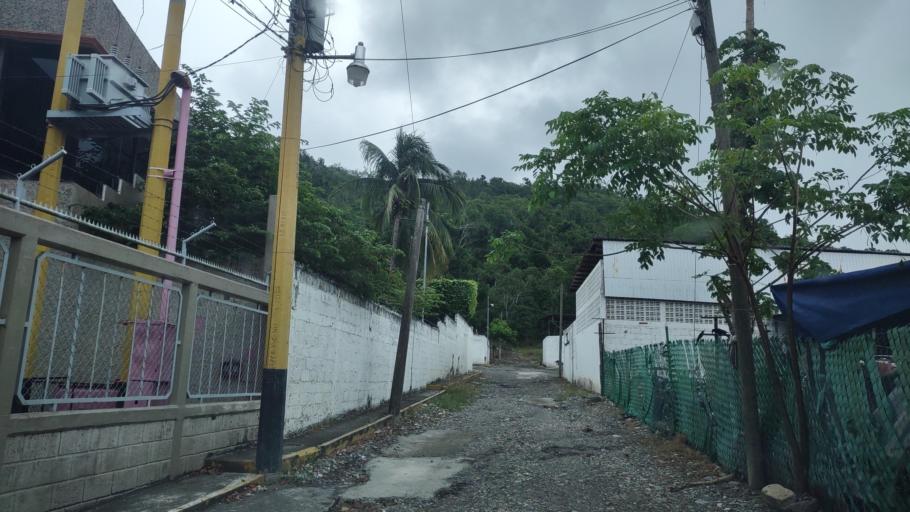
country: MX
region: Veracruz
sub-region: Papantla
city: Fraccionamiento la Florida
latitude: 20.5855
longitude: -97.4236
